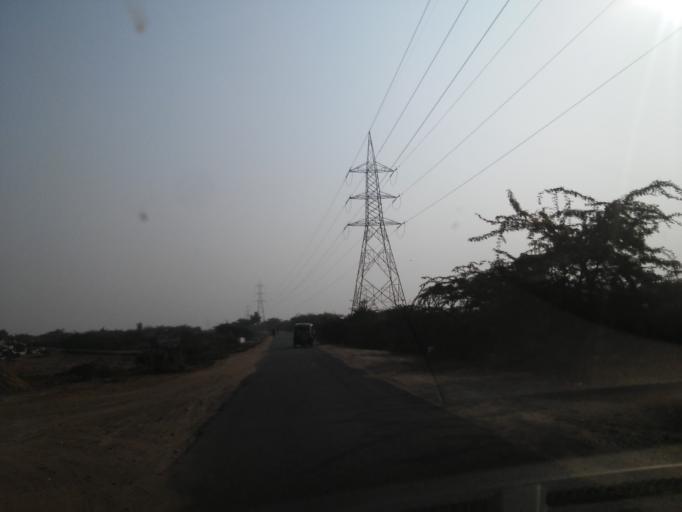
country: IN
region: Gujarat
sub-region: Kachchh
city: Mandvi
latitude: 22.8324
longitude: 69.5055
